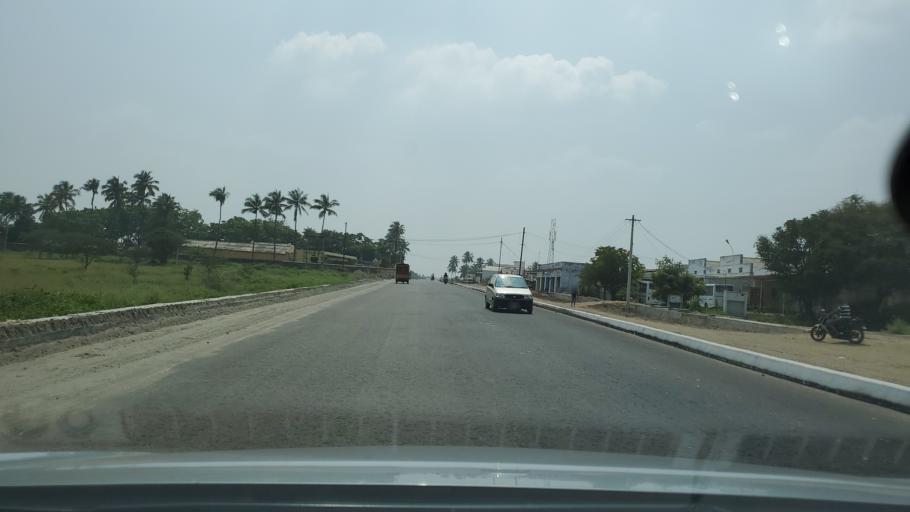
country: IN
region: Tamil Nadu
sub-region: Tiruppur
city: Kangayam
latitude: 10.9500
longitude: 77.4341
